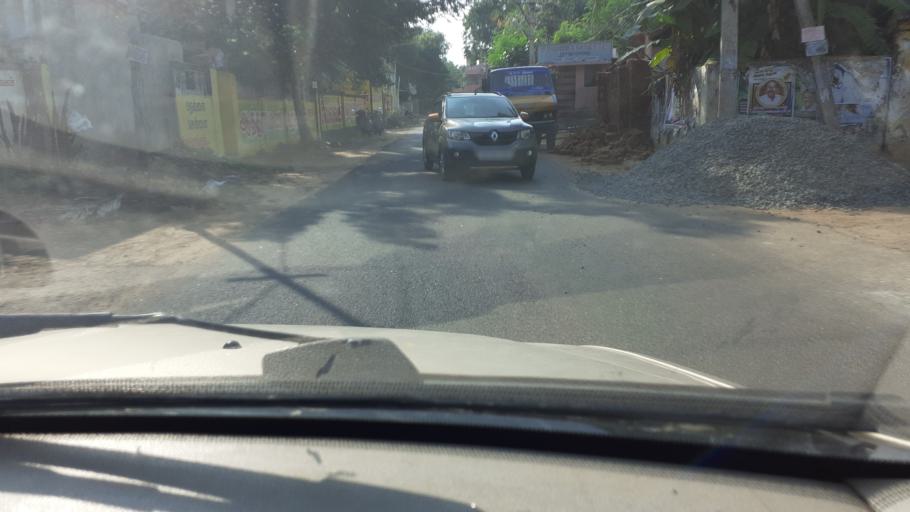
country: IN
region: Tamil Nadu
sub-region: Thoothukkudi
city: Eral
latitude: 8.5790
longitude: 78.0339
